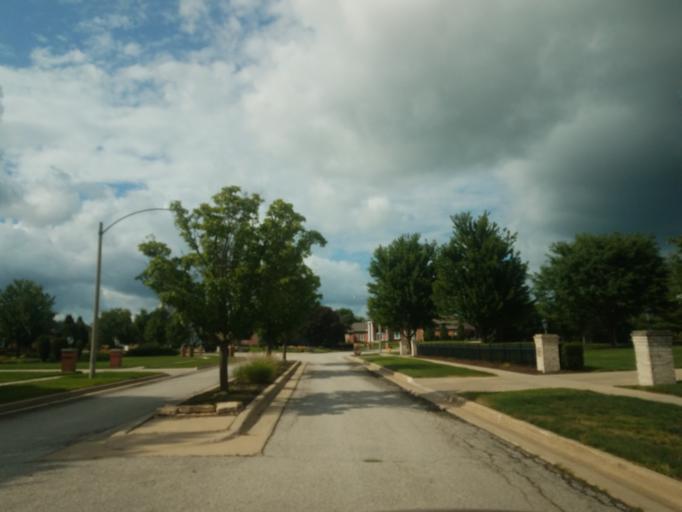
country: US
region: Illinois
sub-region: McLean County
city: Normal
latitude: 40.5082
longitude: -88.9111
